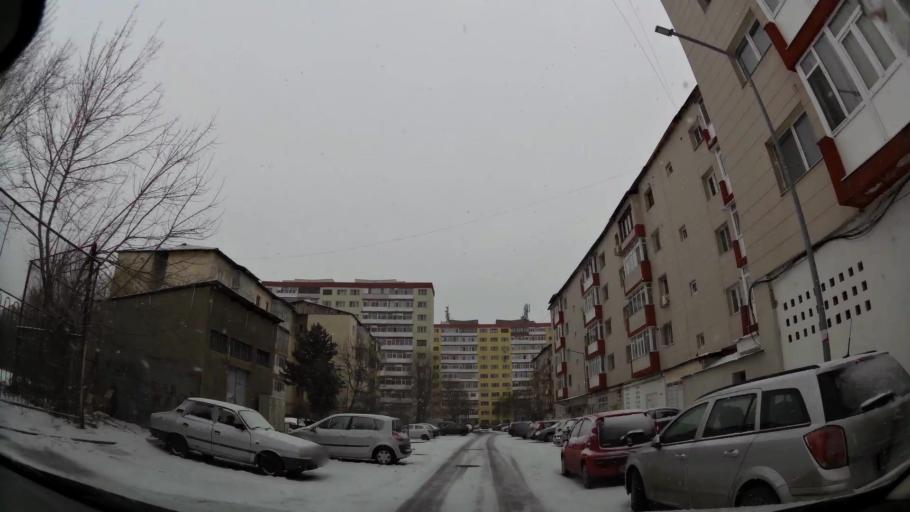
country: RO
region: Dambovita
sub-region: Municipiul Targoviste
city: Targoviste
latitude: 44.9249
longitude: 25.4415
